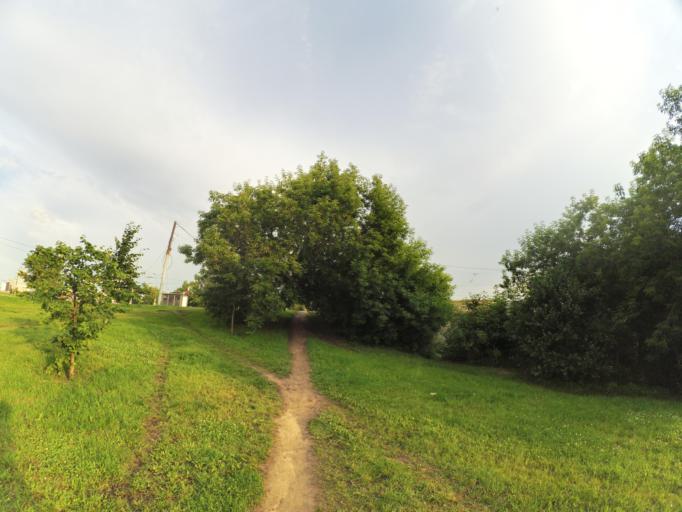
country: RU
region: Moscow
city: Shchukino
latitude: 55.7802
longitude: 37.4482
